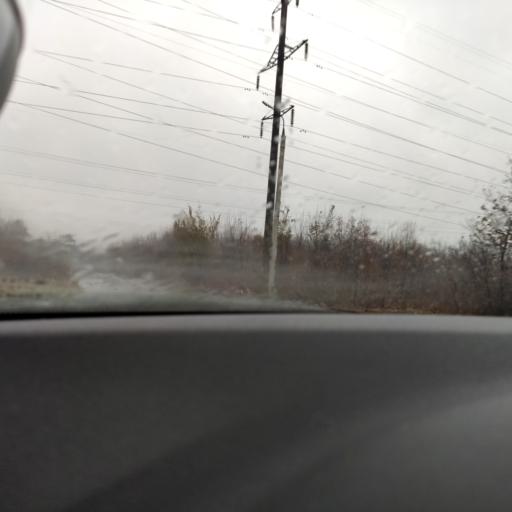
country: RU
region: Samara
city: Petra-Dubrava
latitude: 53.2593
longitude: 50.2842
